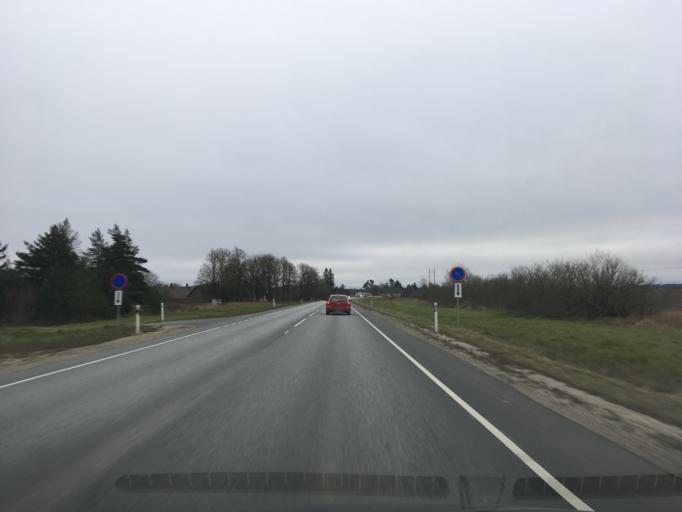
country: EE
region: Laeaene-Virumaa
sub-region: Someru vald
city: Someru
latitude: 59.3786
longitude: 26.4165
